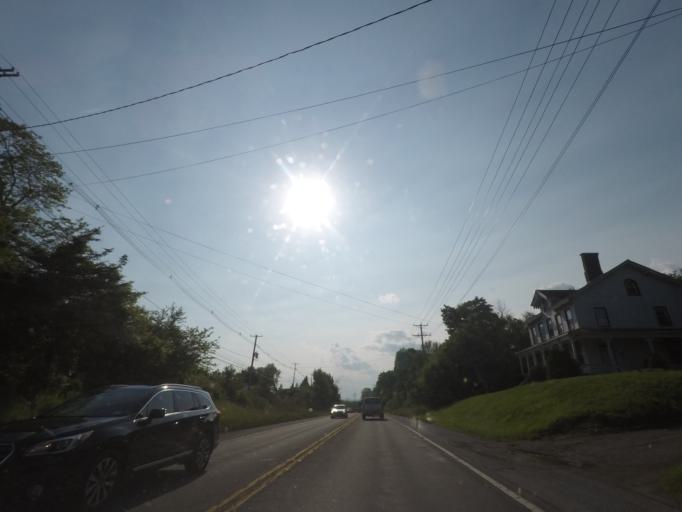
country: US
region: New York
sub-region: Orange County
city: Orange Lake
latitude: 41.5260
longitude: -74.1266
